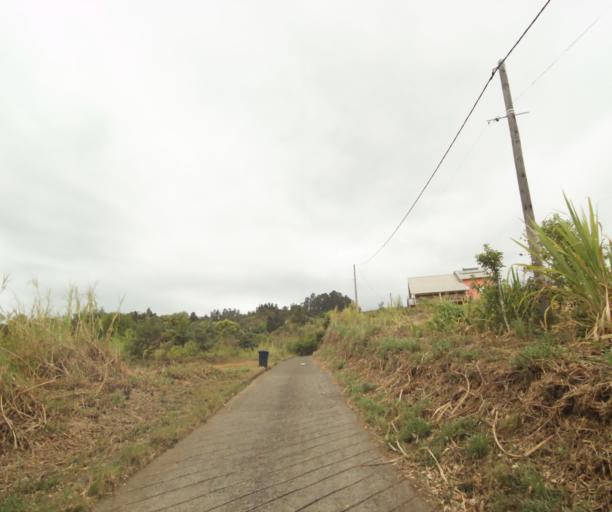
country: RE
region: Reunion
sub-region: Reunion
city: Saint-Paul
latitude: -21.0158
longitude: 55.3326
